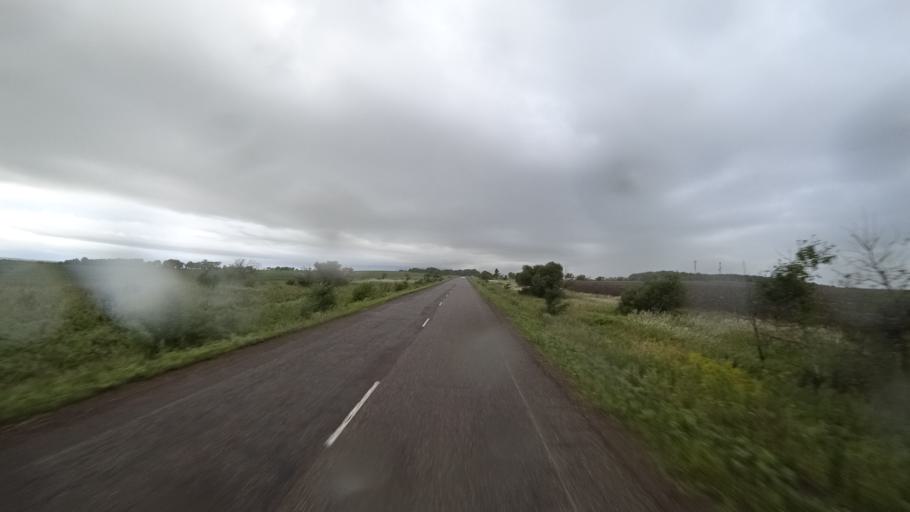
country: RU
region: Primorskiy
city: Chernigovka
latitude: 44.3647
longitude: 132.5418
